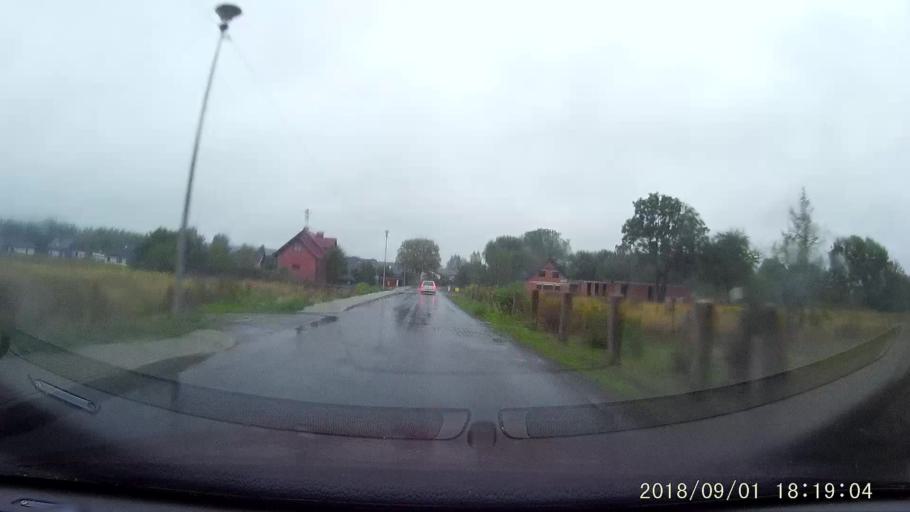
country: PL
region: Lower Silesian Voivodeship
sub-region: Powiat zgorzelecki
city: Piensk
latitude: 51.2567
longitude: 15.0459
